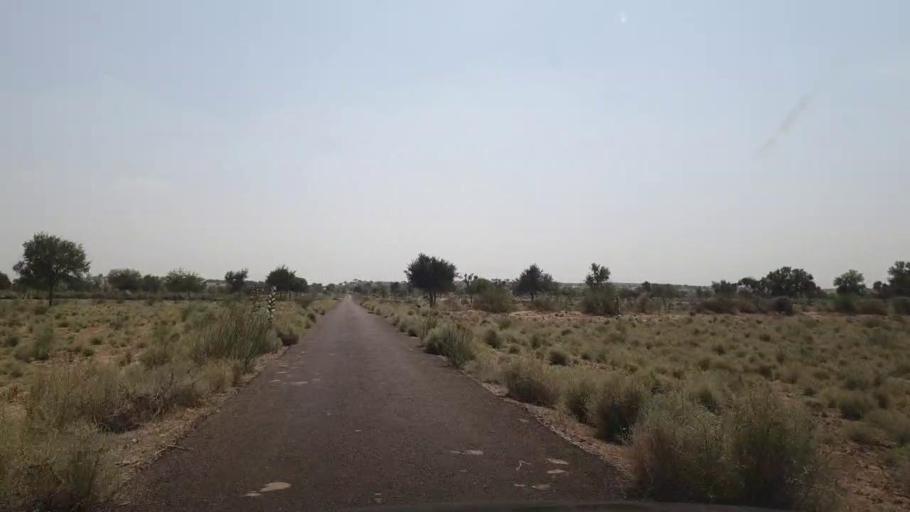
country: PK
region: Sindh
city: Islamkot
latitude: 25.0890
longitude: 70.7337
